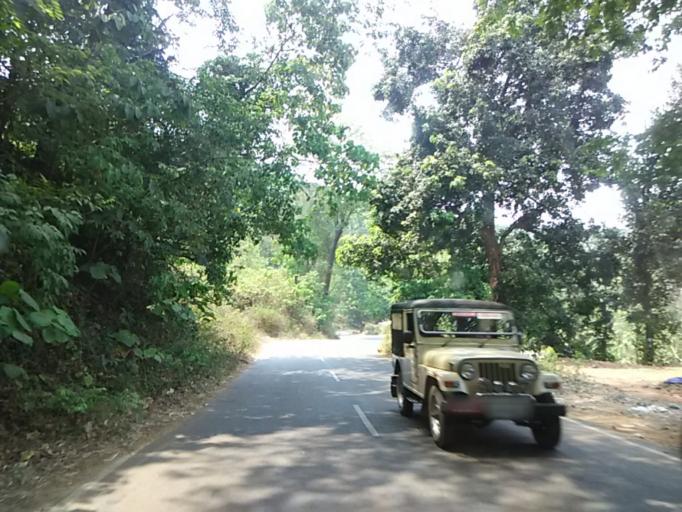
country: IN
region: Karnataka
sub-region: Kodagu
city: Virarajendrapet
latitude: 12.0611
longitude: 75.7221
